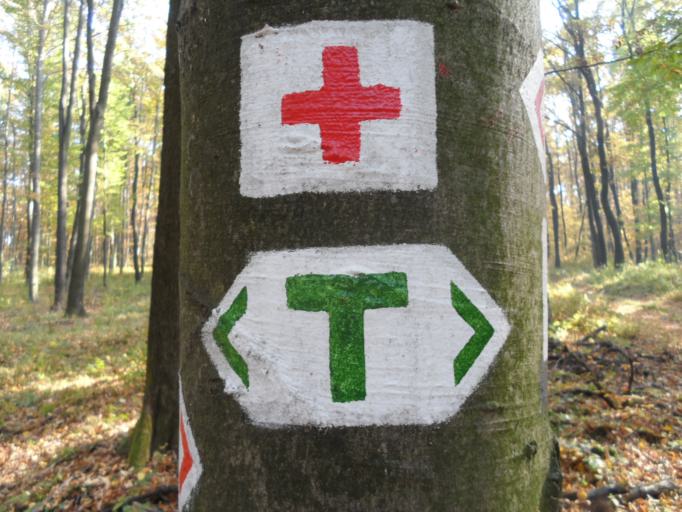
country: HU
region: Veszprem
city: Herend
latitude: 47.1967
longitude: 17.6593
